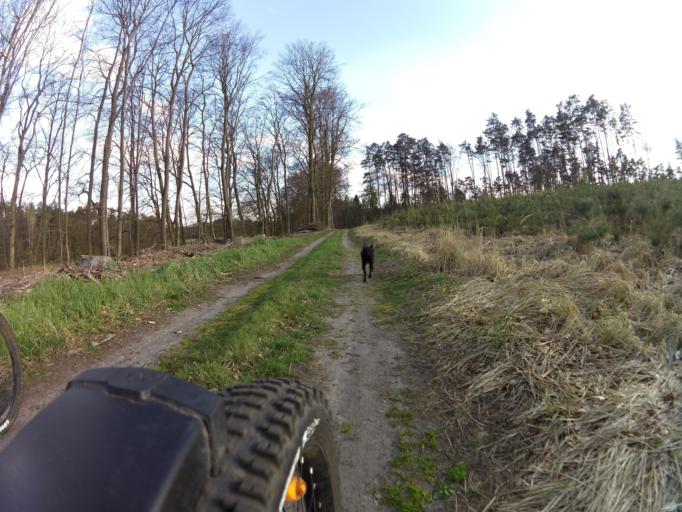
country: PL
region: West Pomeranian Voivodeship
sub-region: Powiat gryficki
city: Ploty
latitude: 53.7573
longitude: 15.2694
